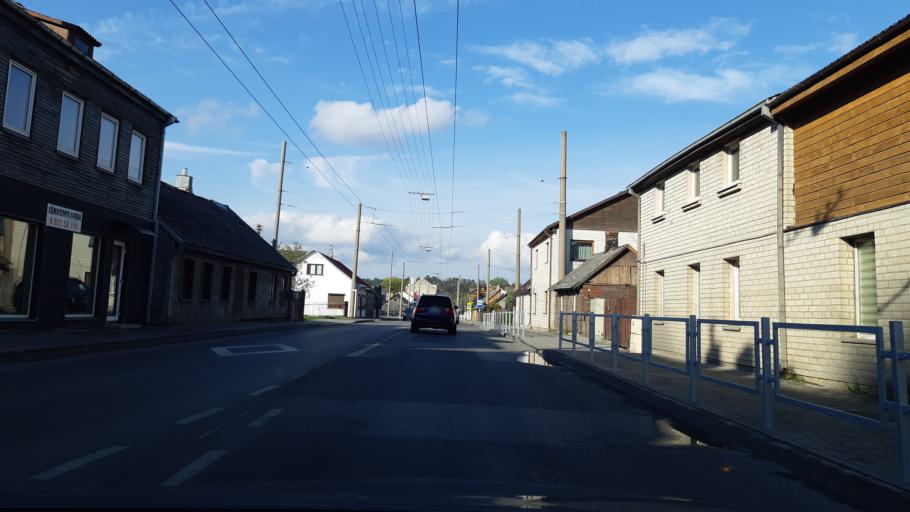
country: LT
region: Kauno apskritis
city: Dainava (Kaunas)
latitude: 54.8648
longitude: 23.9663
